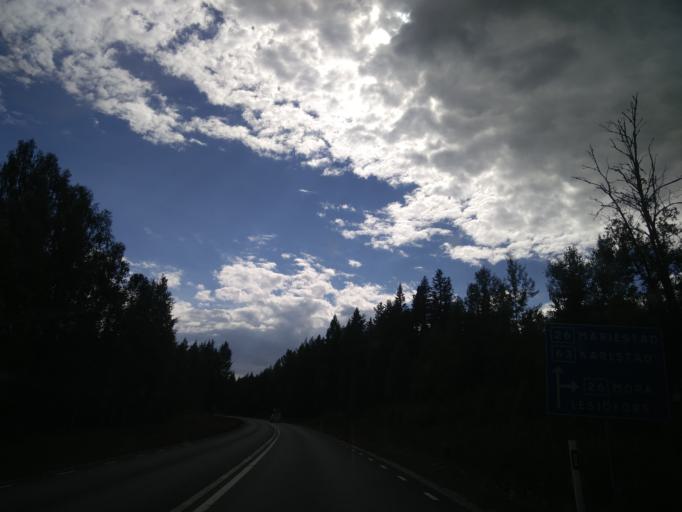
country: SE
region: Vaermland
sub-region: Filipstads Kommun
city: Filipstad
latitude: 59.7723
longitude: 14.2633
